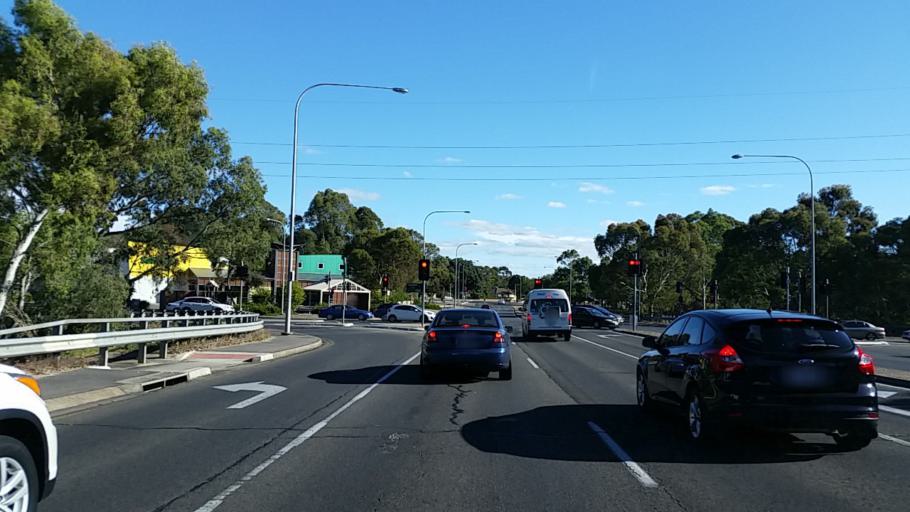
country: AU
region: South Australia
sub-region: Tea Tree Gully
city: Modbury
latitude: -34.8333
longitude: 138.6805
